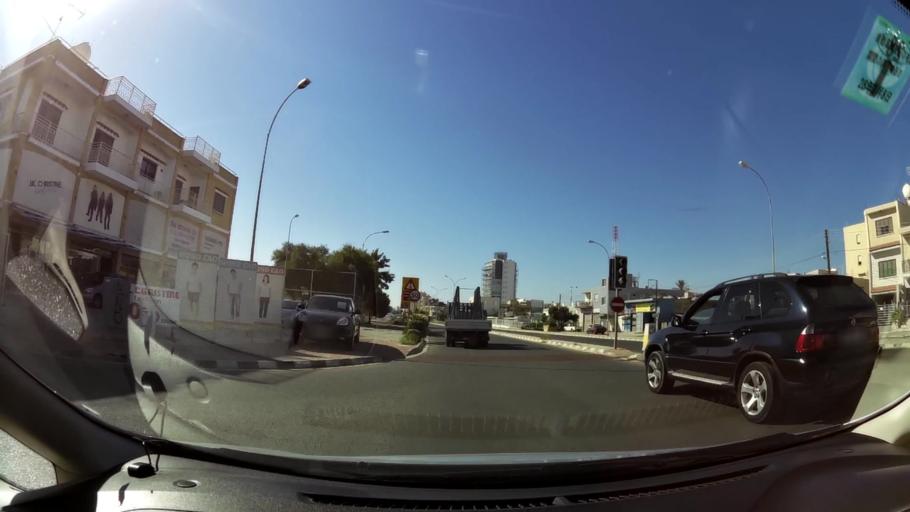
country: CY
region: Larnaka
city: Larnaca
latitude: 34.9337
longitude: 33.6285
